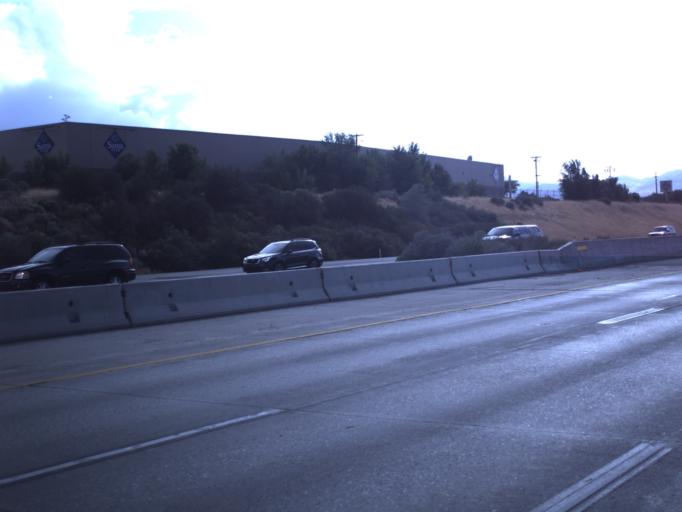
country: US
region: Utah
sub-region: Salt Lake County
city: Midvale
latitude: 40.6314
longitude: -111.8848
